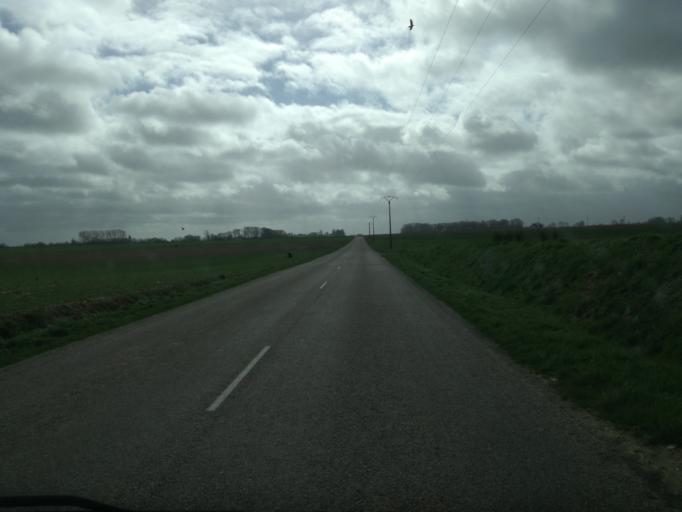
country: FR
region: Haute-Normandie
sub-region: Departement de la Seine-Maritime
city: Valliquerville
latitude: 49.6064
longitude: 0.6668
